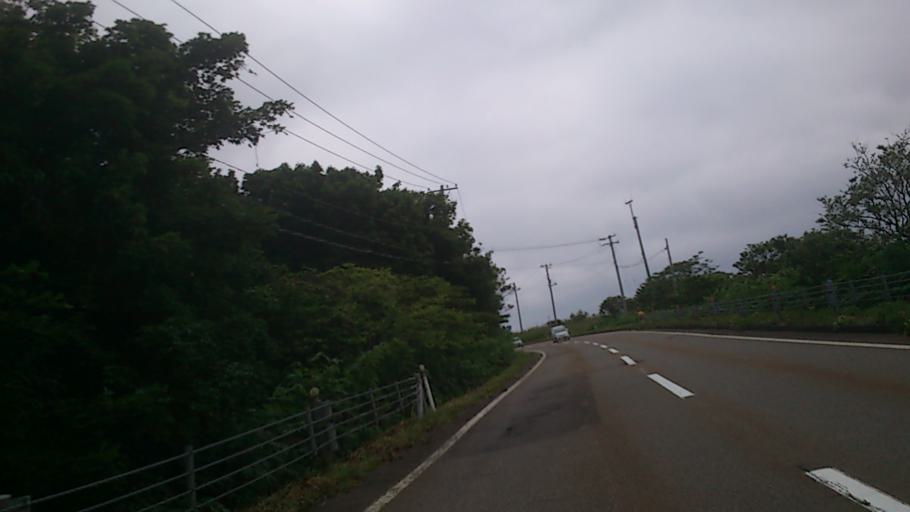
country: JP
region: Hokkaido
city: Kamiiso
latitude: 41.6910
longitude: 140.0135
